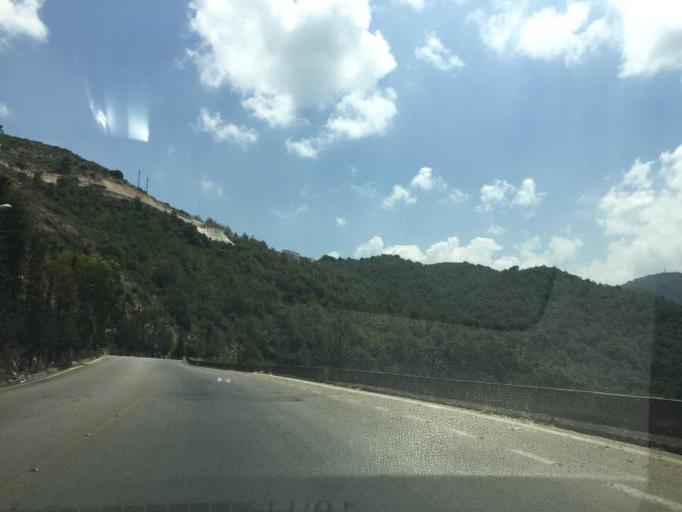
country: LB
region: Mont-Liban
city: Beit ed Dine
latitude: 33.7048
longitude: 35.4648
